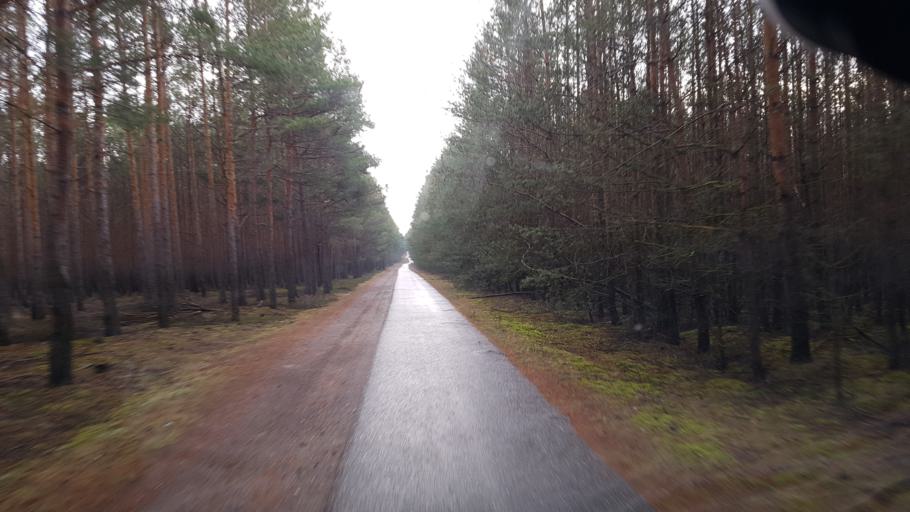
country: DE
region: Brandenburg
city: Hohenbucko
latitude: 51.7551
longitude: 13.4301
